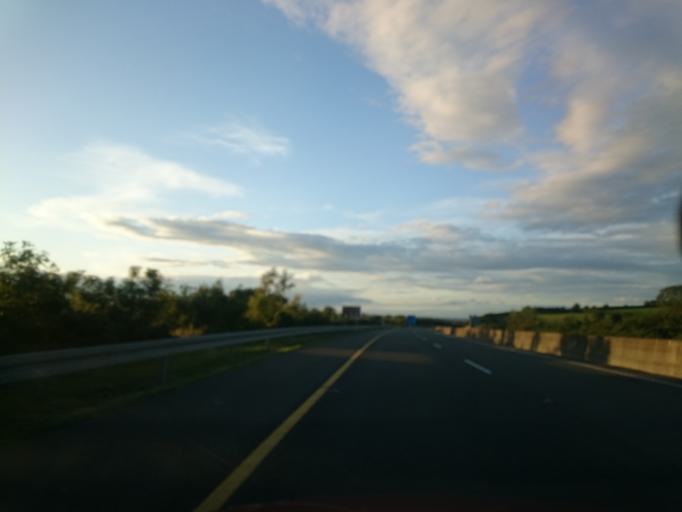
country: IE
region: Leinster
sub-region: Loch Garman
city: Gorey
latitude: 52.7017
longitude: -6.2626
